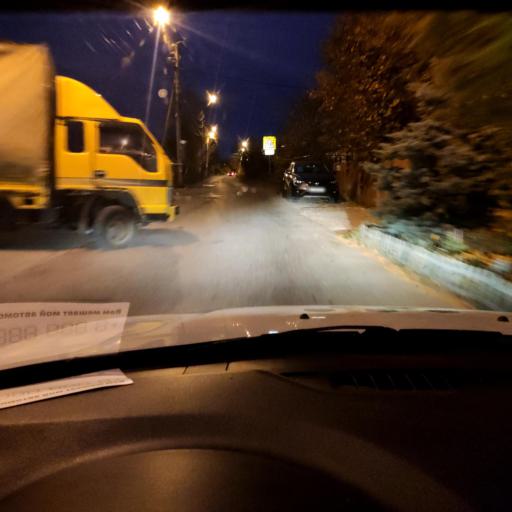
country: RU
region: Samara
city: Tol'yatti
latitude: 53.5359
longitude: 49.4028
